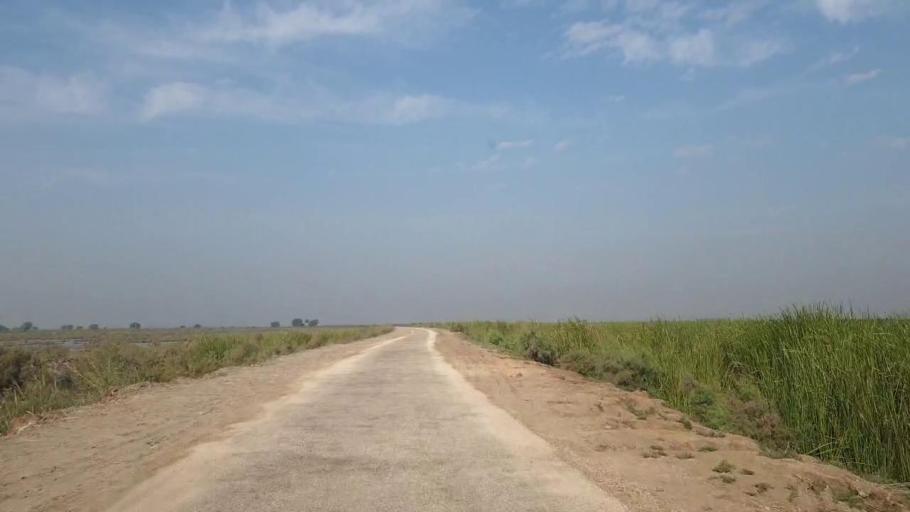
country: PK
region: Sindh
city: Tando Bago
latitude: 24.8441
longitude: 68.9780
